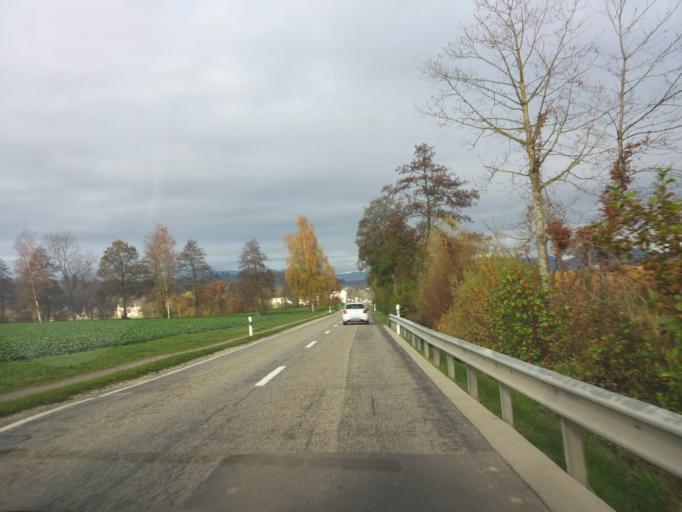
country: CH
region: Bern
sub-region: Oberaargau
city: Roggwil
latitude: 47.2227
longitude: 7.8494
